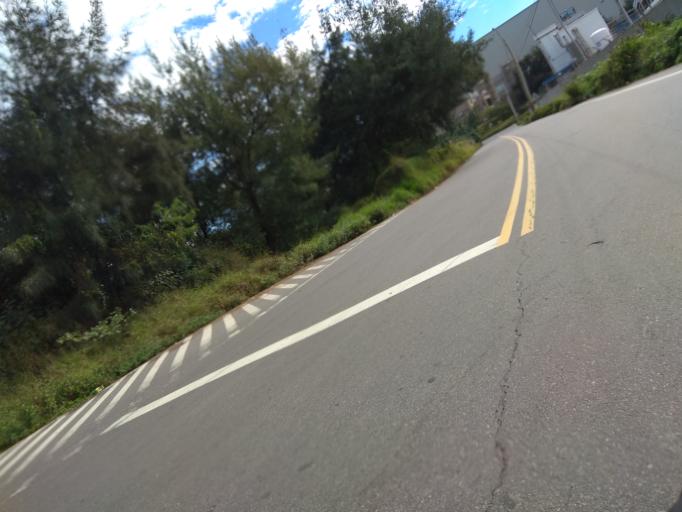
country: TW
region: Taiwan
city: Taoyuan City
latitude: 25.0564
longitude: 121.1020
